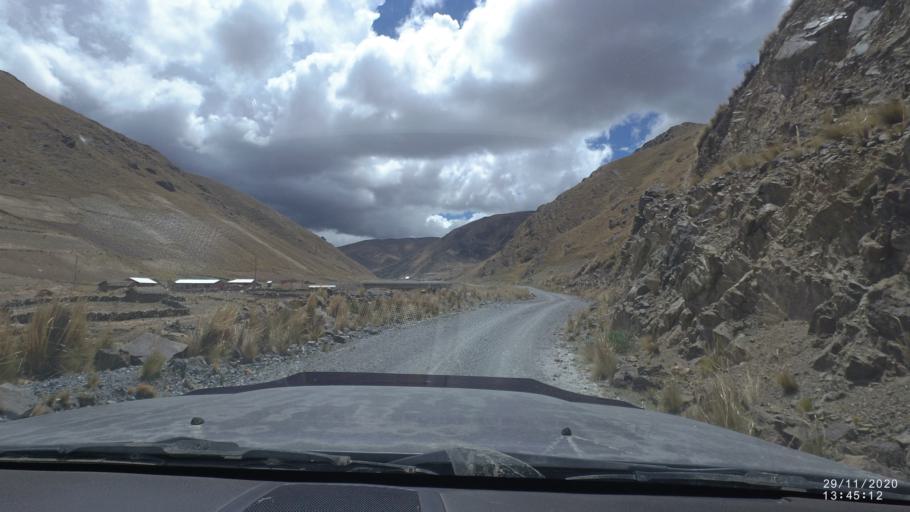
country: BO
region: Cochabamba
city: Cochabamba
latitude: -17.1487
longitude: -66.3196
